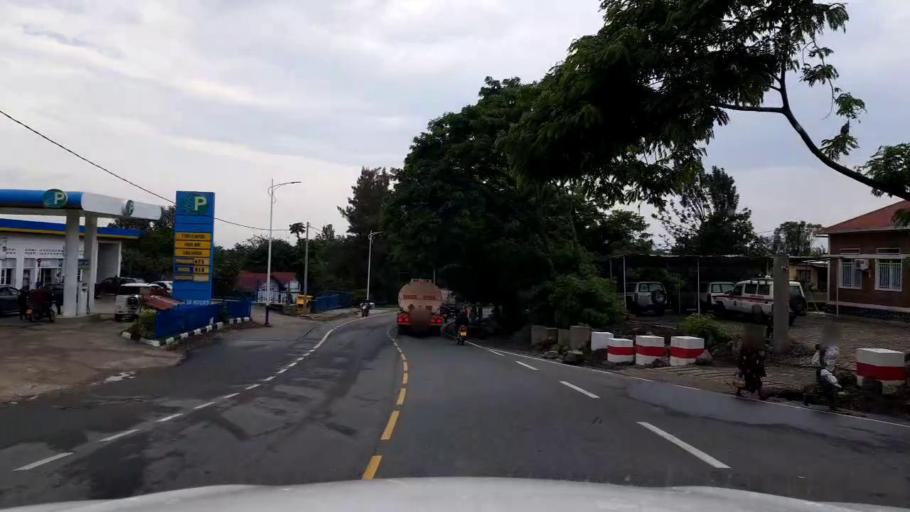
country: RW
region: Western Province
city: Gisenyi
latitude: -1.7029
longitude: 29.2626
